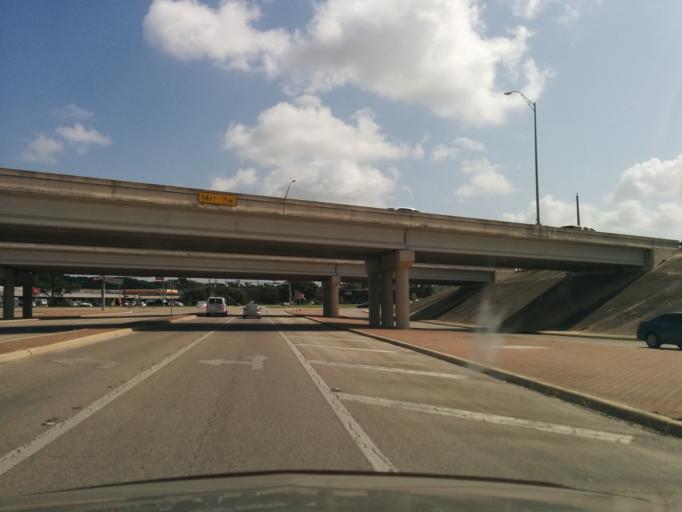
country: US
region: Texas
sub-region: Bexar County
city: Helotes
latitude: 29.5866
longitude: -98.6313
